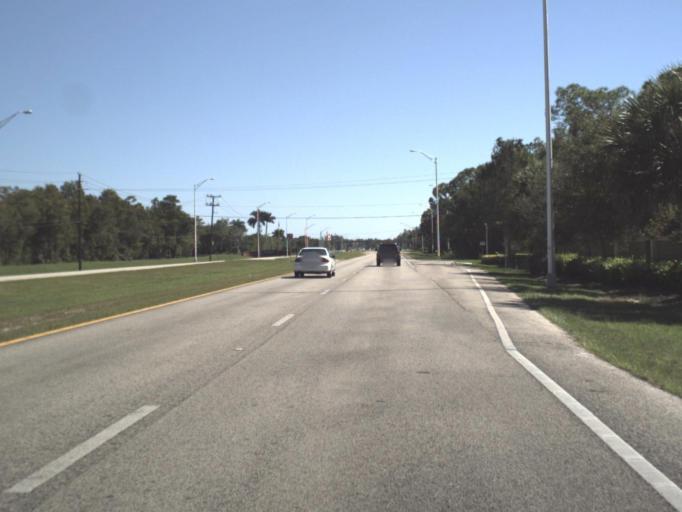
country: US
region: Florida
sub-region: Collier County
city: Lely
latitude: 26.1387
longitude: -81.7260
